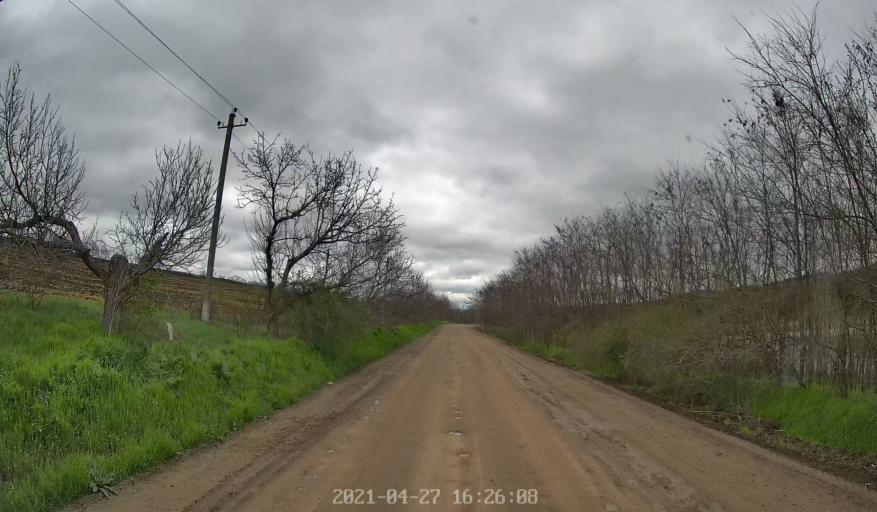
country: MD
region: Chisinau
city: Singera
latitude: 46.9812
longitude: 29.0237
